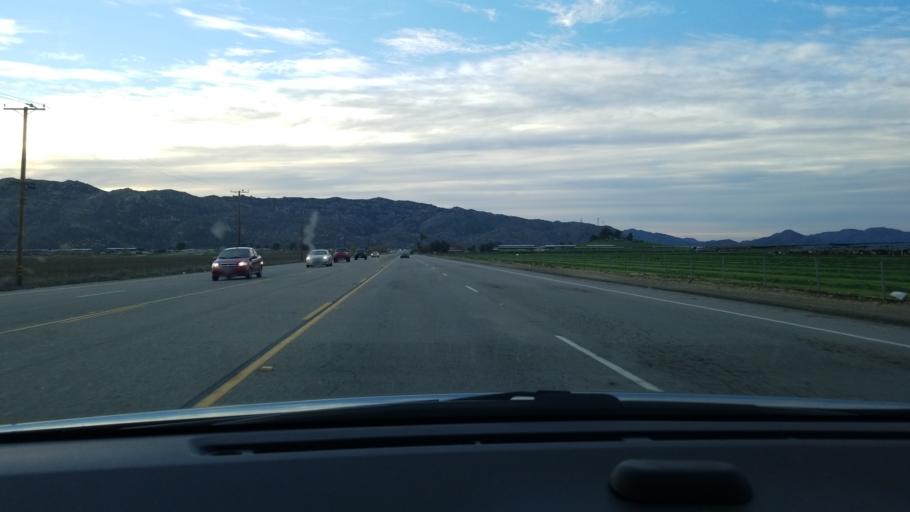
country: US
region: California
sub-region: Riverside County
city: San Jacinto
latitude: 33.8235
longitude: -117.0169
